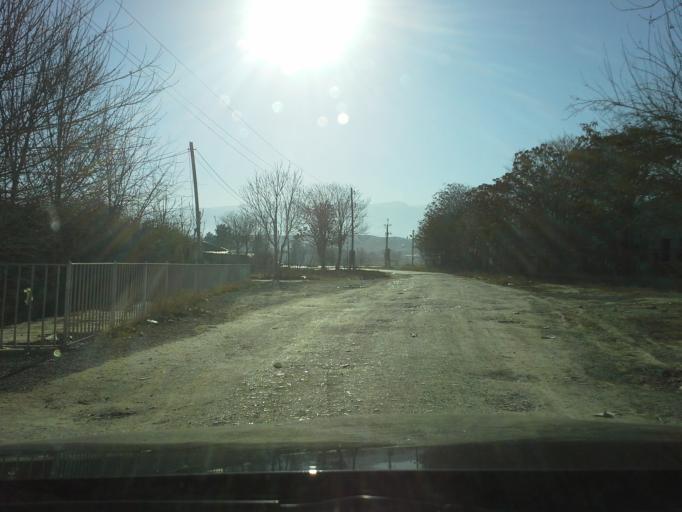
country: TM
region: Ahal
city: Ashgabat
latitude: 37.9668
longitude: 58.3366
